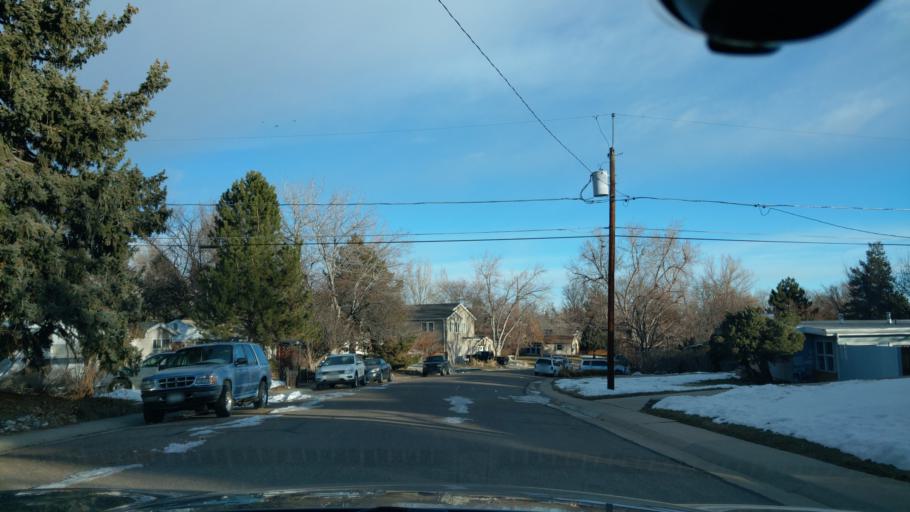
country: US
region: Colorado
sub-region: Jefferson County
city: Lakewood
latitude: 39.7293
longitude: -105.1129
